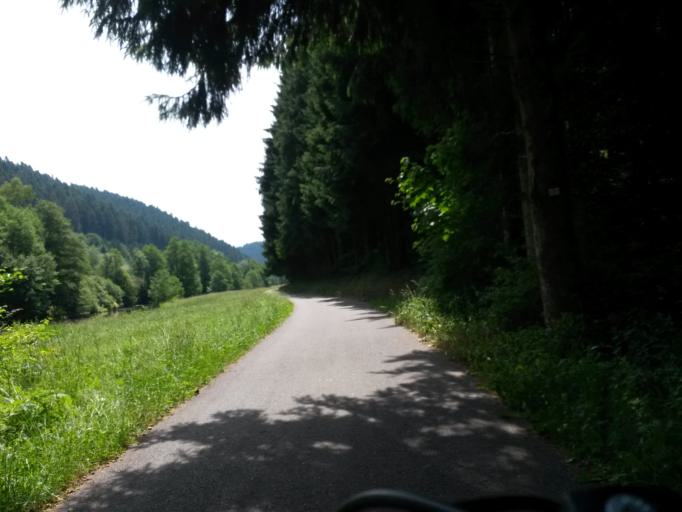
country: DE
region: Baden-Wuerttemberg
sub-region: Karlsruhe Region
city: Neubulach
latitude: 48.6523
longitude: 8.7247
